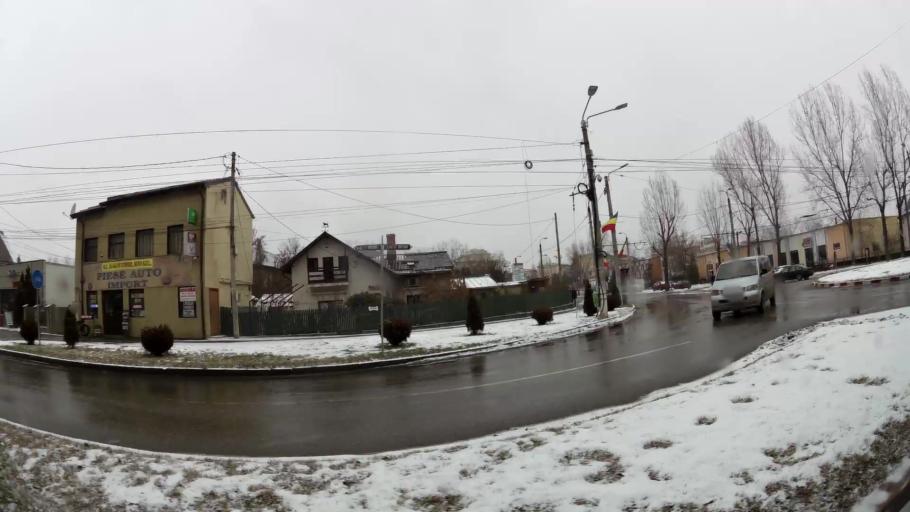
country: RO
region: Dambovita
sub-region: Municipiul Targoviste
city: Targoviste
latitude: 44.9175
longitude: 25.4674
